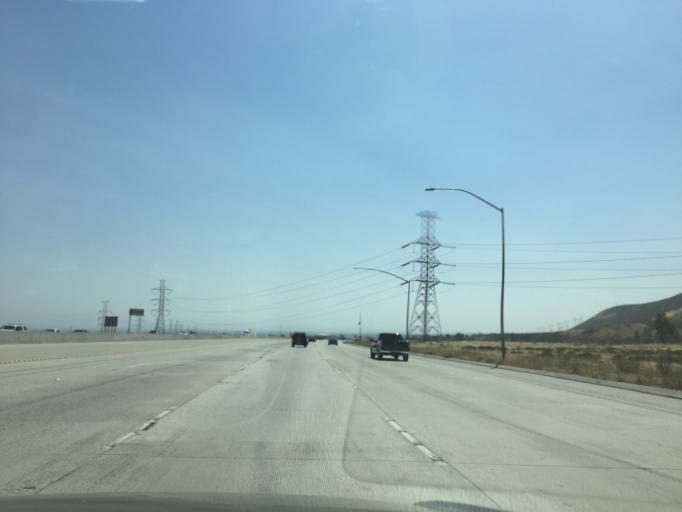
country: US
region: California
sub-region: San Bernardino County
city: Fontana
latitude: 34.1795
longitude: -117.4397
